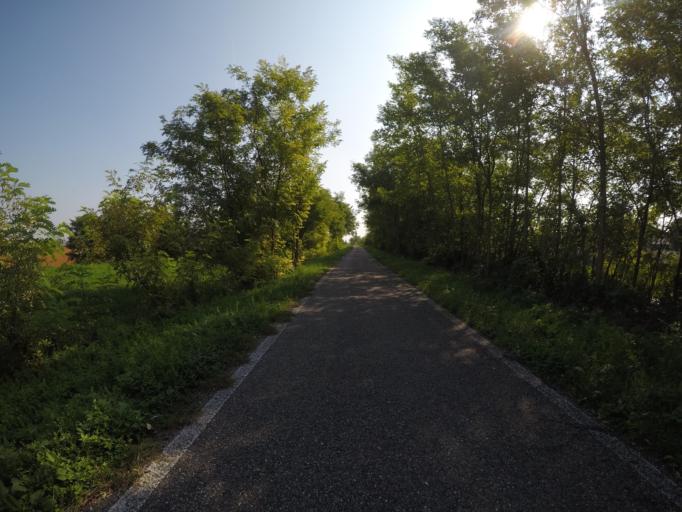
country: IT
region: Veneto
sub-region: Provincia di Rovigo
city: Frassinelle Polesine
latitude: 44.9949
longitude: 11.7093
